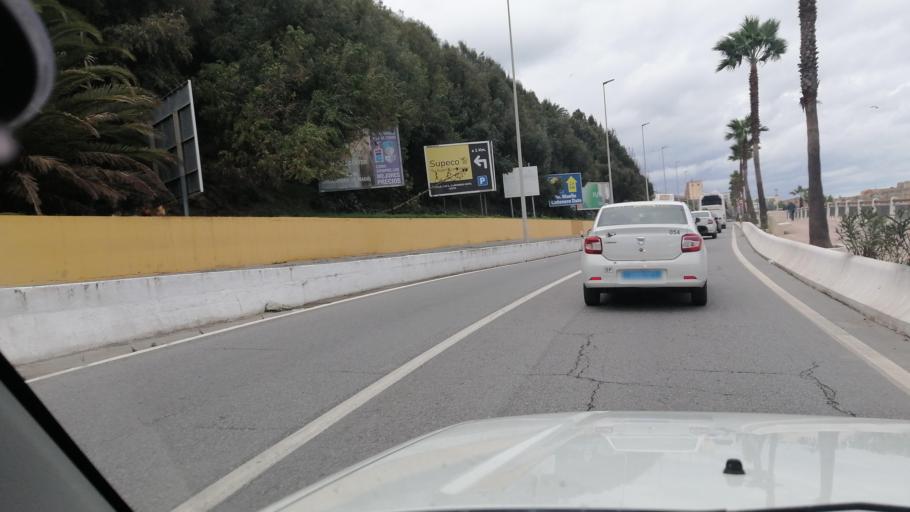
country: ES
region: Ceuta
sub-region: Ceuta
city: Ceuta
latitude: 35.8831
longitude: -5.3245
